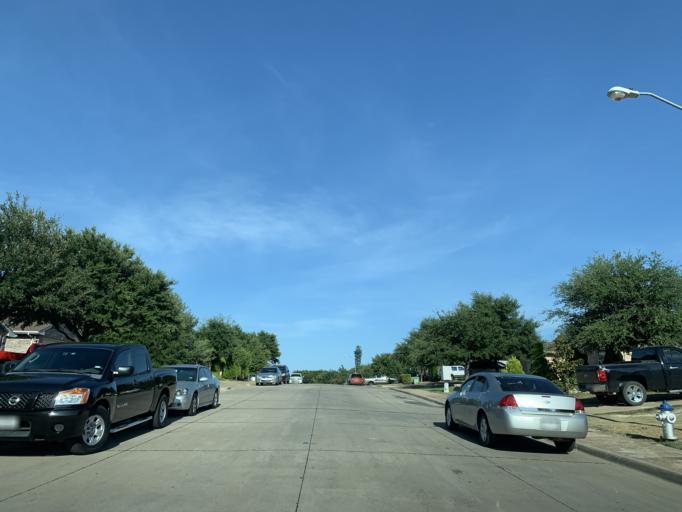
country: US
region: Texas
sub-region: Dallas County
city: Cockrell Hill
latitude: 32.7076
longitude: -96.8861
